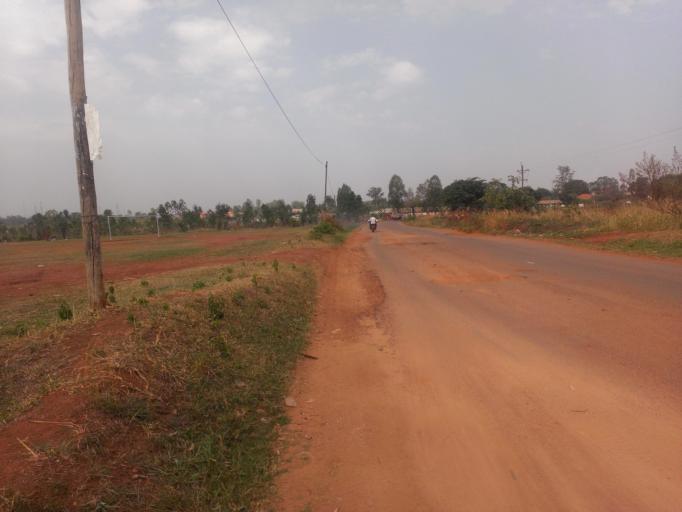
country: UG
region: Northern Region
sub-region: Gulu District
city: Gulu
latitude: 2.7850
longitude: 32.3117
